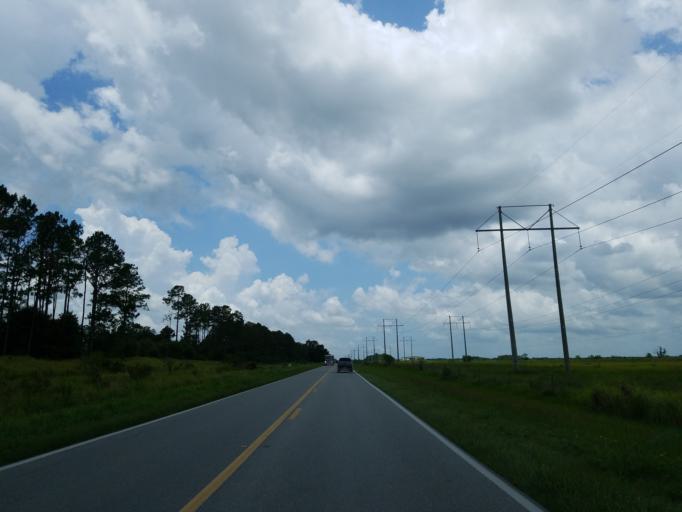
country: US
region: Florida
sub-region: Polk County
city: Willow Oak
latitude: 27.8507
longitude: -82.0404
